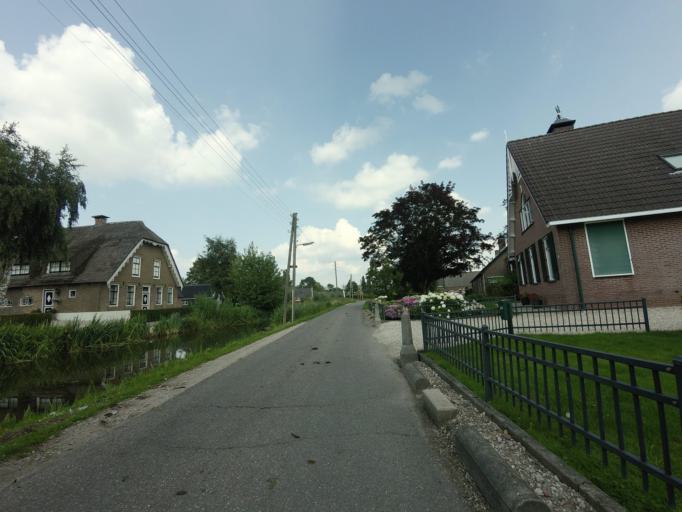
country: NL
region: South Holland
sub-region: Gemeente Gouda
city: Gouda
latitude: 51.9866
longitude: 4.7360
